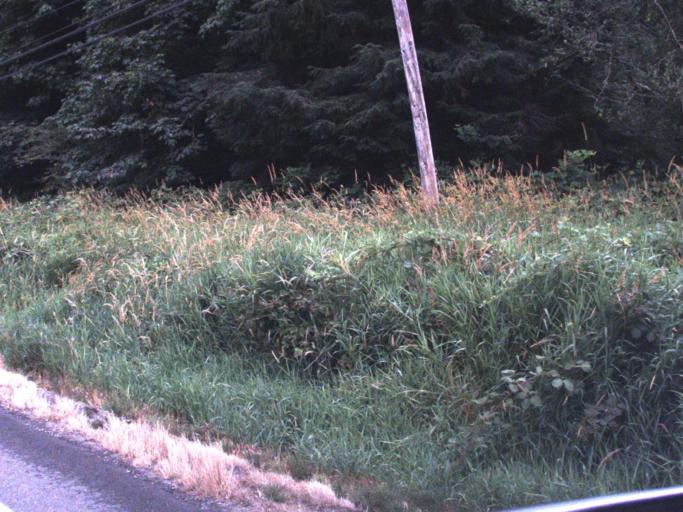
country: US
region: Washington
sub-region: King County
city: Union Hill-Novelty Hill
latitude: 47.6410
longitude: -122.0130
